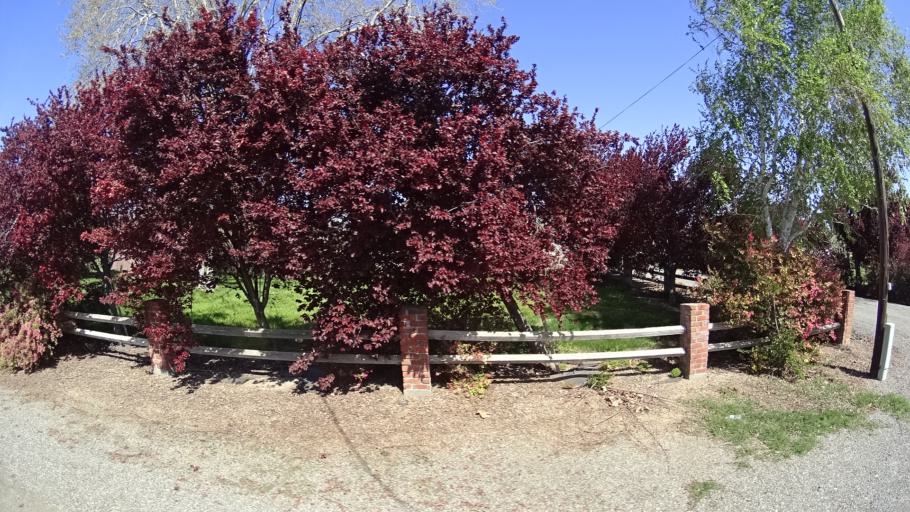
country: US
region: California
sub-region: Glenn County
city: Orland
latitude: 39.7897
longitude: -122.1190
